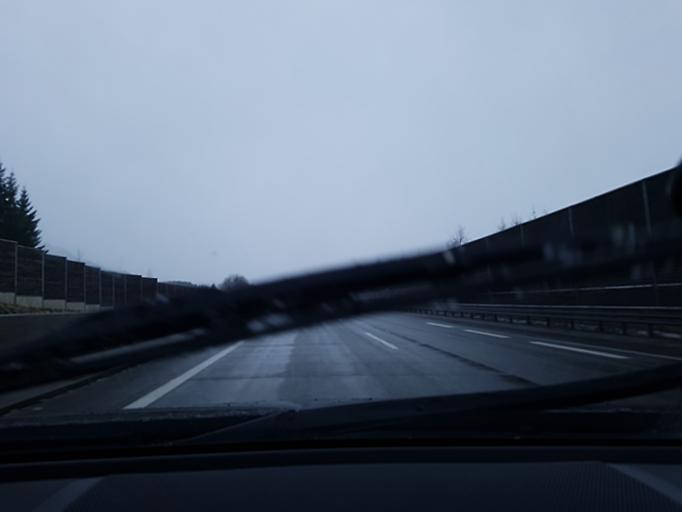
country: AT
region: Salzburg
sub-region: Politischer Bezirk Hallein
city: Golling an der Salzach
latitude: 47.5979
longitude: 13.1511
